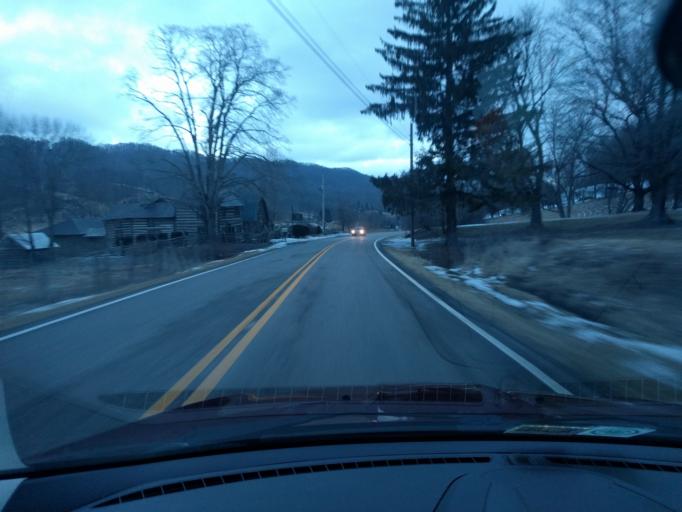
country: US
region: Virginia
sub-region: Alleghany County
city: Clifton Forge
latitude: 37.9208
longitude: -79.8907
